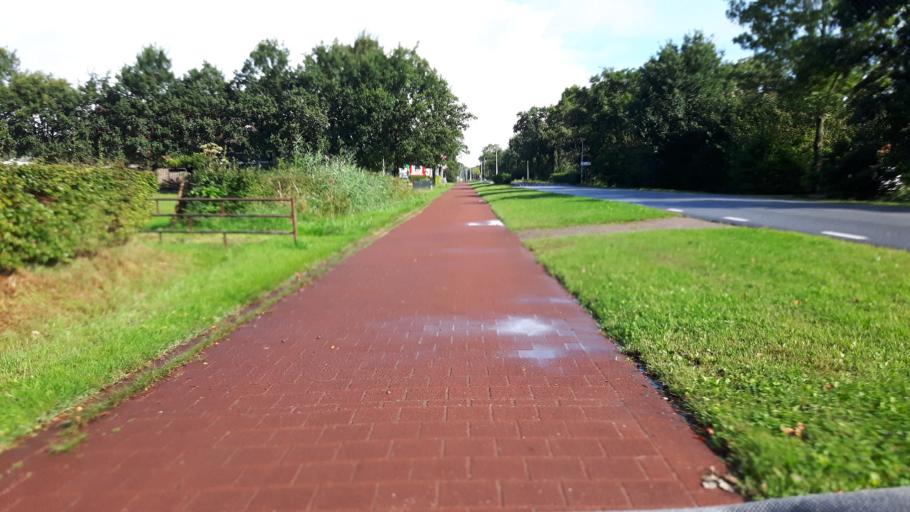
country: NL
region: Friesland
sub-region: Gemeente Smallingerland
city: Drachten
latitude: 53.0843
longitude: 6.0998
